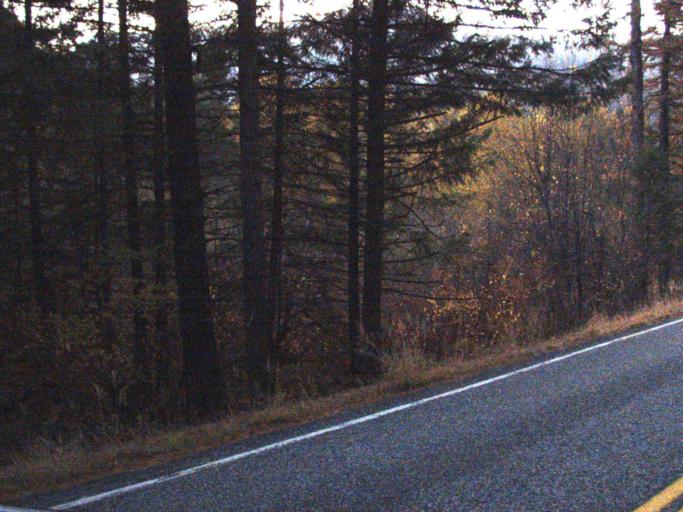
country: US
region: Washington
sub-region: Ferry County
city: Republic
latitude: 48.3692
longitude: -118.7491
